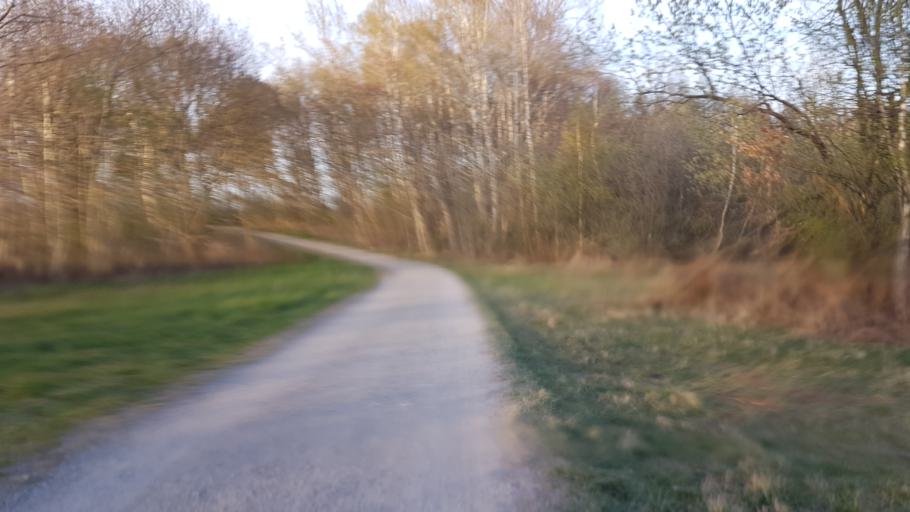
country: DE
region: Lower Saxony
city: Isernhagen Farster Bauerschaft
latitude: 52.4214
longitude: 9.8560
